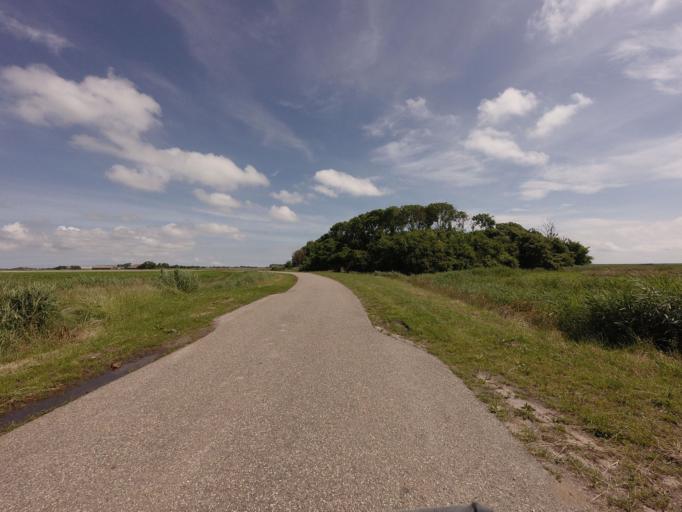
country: NL
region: North Holland
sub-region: Gemeente Texel
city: Den Burg
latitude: 53.0599
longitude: 4.8481
